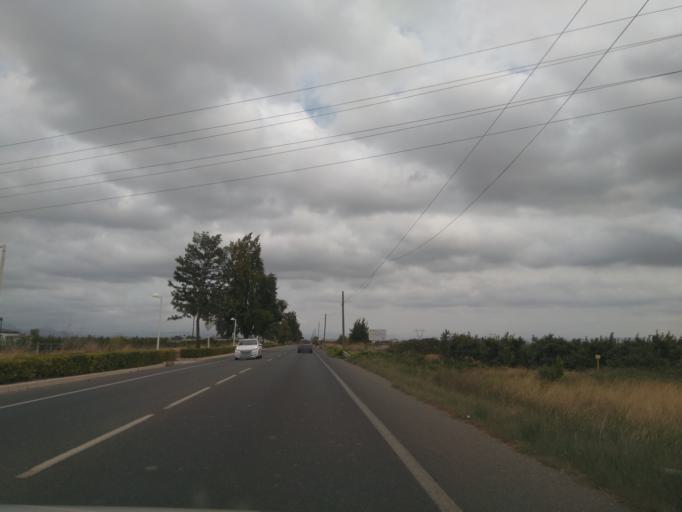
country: ES
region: Valencia
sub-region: Provincia de Valencia
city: Carlet
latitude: 39.2154
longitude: -0.5148
